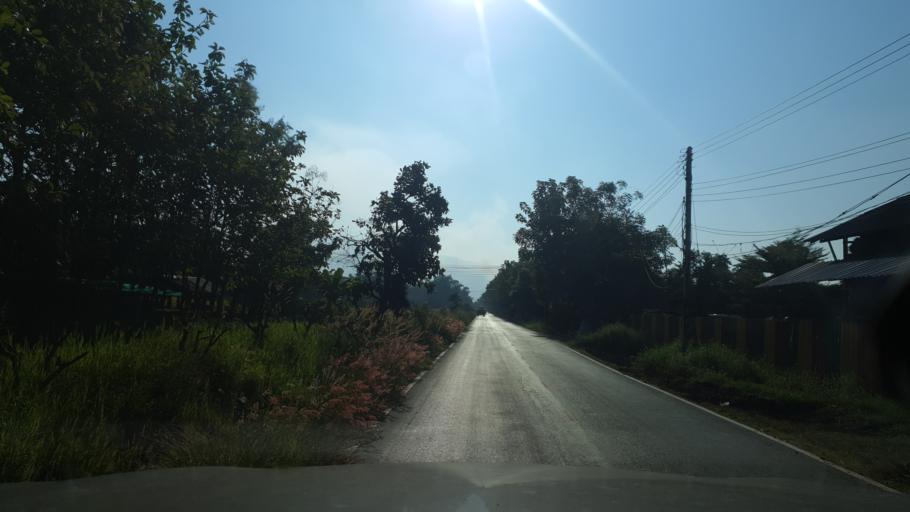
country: TH
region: Chiang Mai
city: San Kamphaeng
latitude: 18.6951
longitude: 99.1511
